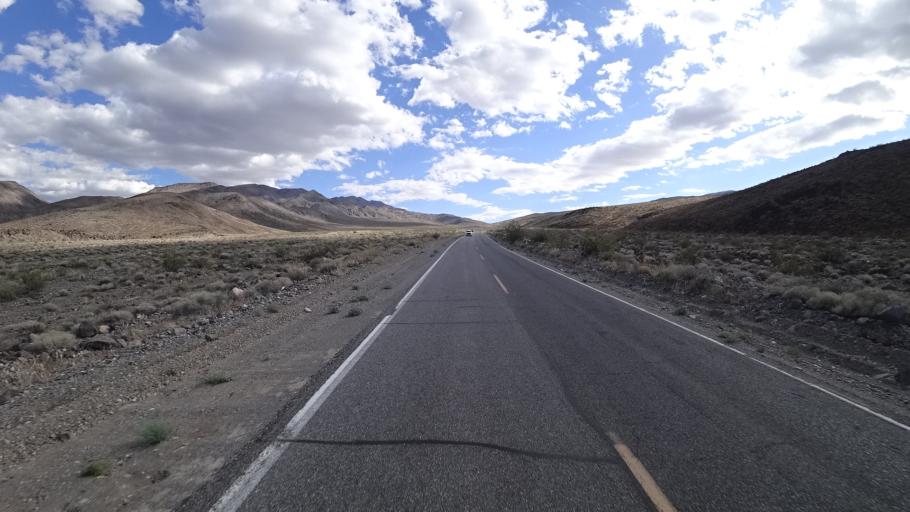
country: US
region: Nevada
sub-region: Nye County
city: Beatty
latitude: 36.4583
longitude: -117.2386
